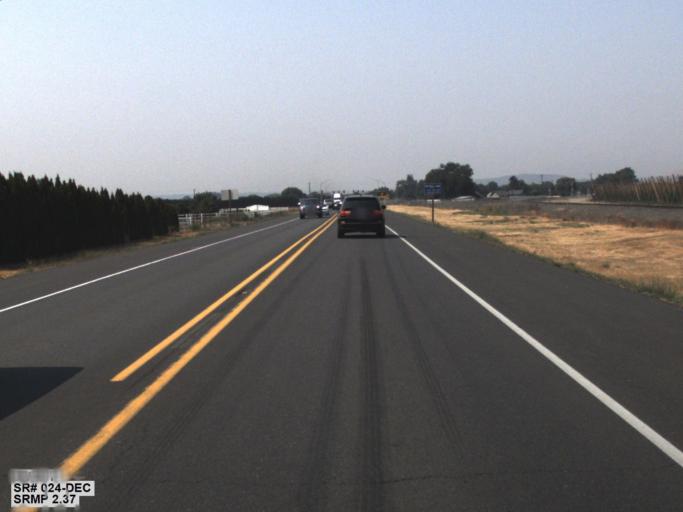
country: US
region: Washington
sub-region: Yakima County
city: Terrace Heights
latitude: 46.5725
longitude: -120.4301
